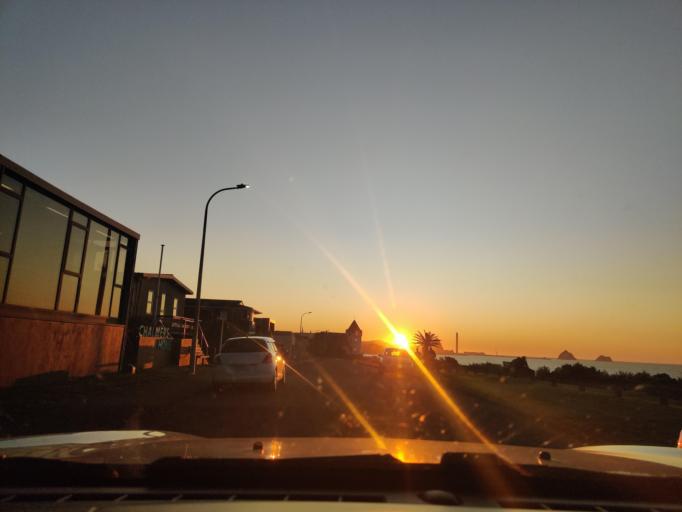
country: NZ
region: Taranaki
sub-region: New Plymouth District
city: New Plymouth
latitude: -39.0514
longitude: 174.0828
